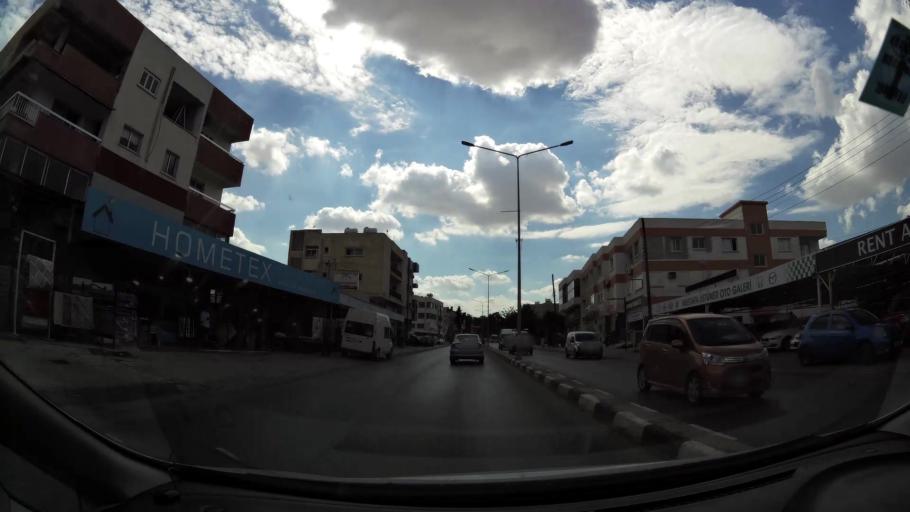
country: CY
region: Lefkosia
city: Nicosia
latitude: 35.1984
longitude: 33.3677
